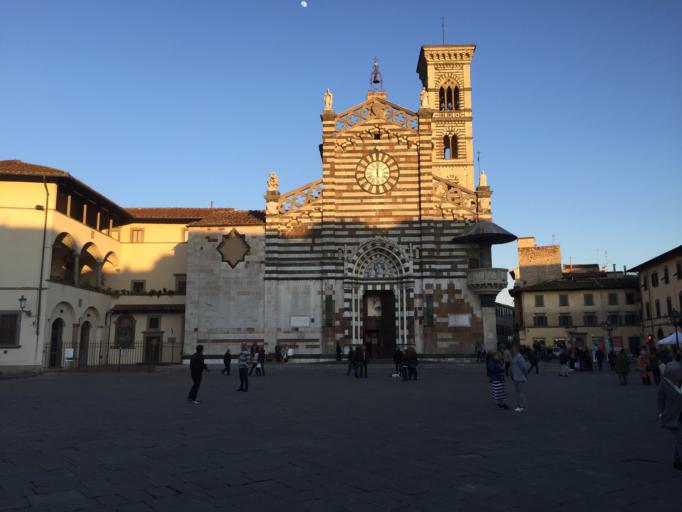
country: IT
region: Tuscany
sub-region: Provincia di Prato
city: Prato
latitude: 43.8821
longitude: 11.0973
